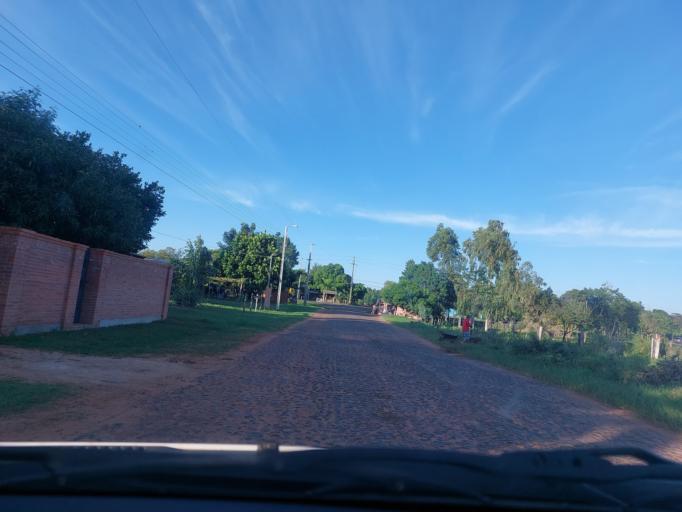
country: PY
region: San Pedro
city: Itacurubi del Rosario
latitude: -24.5911
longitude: -56.6029
